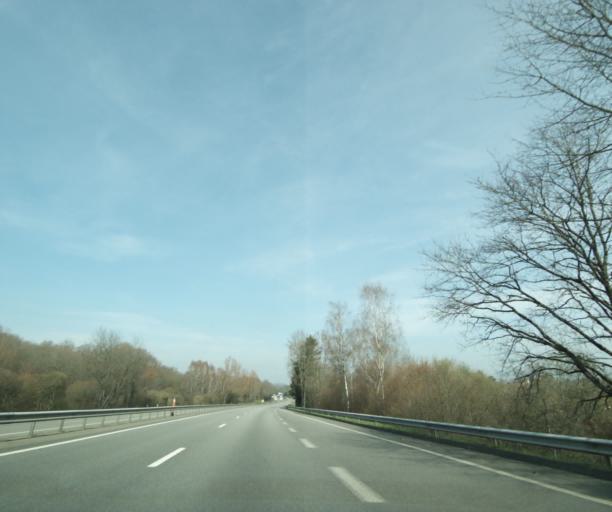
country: FR
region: Limousin
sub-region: Departement de la Haute-Vienne
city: Condat-sur-Vienne
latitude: 45.7850
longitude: 1.3032
